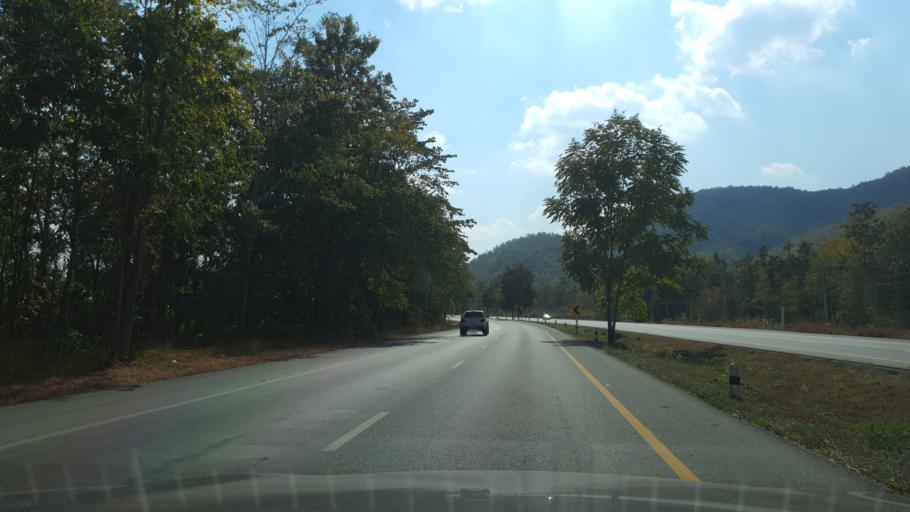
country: TH
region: Lampang
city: Mae Phrik
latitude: 17.3443
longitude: 99.1496
